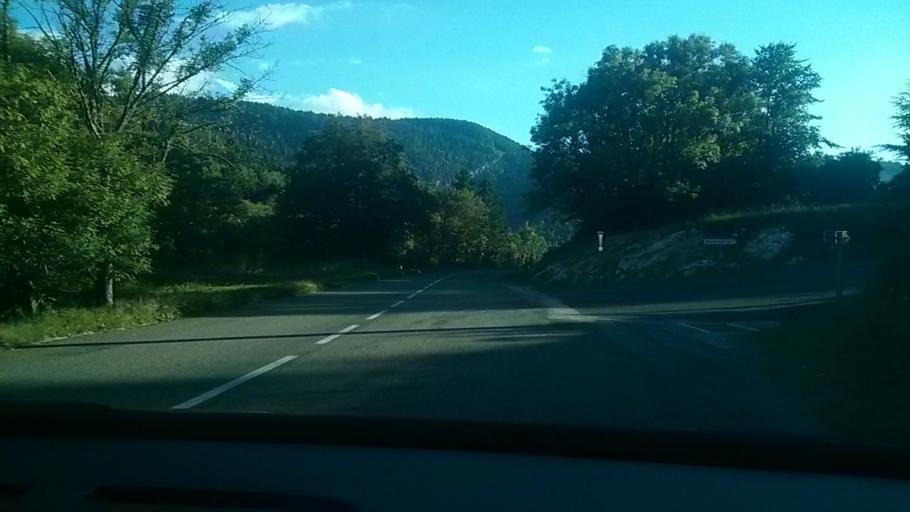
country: FR
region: Franche-Comte
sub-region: Departement du Jura
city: Saint-Claude
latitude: 46.3640
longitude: 5.9118
